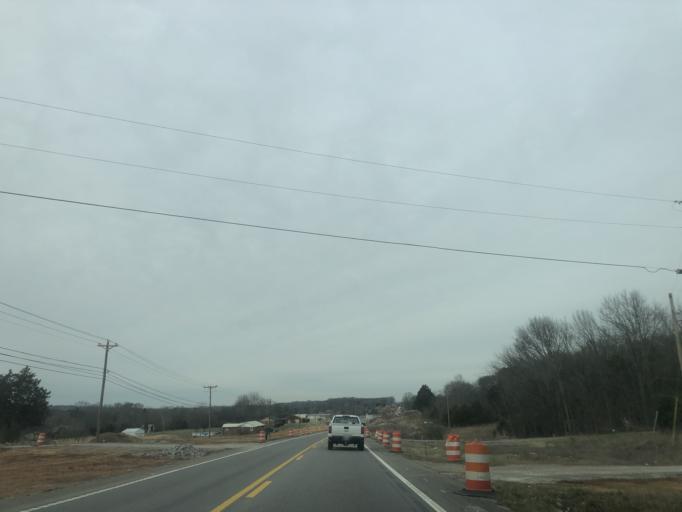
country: US
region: Tennessee
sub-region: Wilson County
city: Mount Juliet
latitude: 36.2600
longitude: -86.4391
